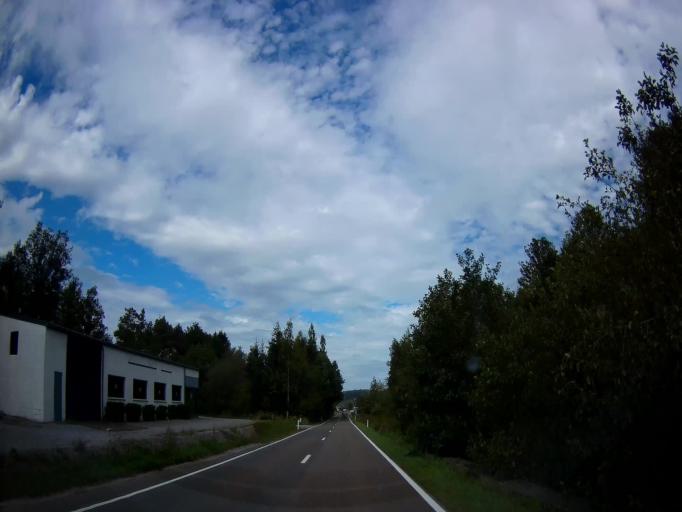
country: BE
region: Wallonia
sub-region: Province du Luxembourg
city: Durbuy
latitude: 50.3381
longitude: 5.4843
